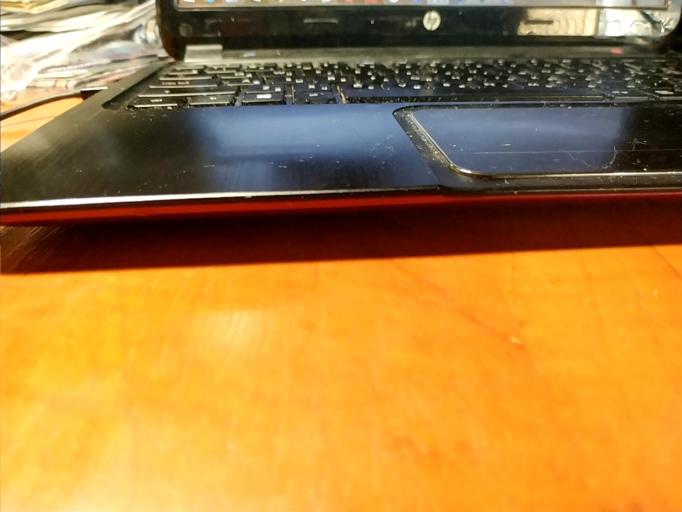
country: RU
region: Republic of Karelia
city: Belomorsk
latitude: 64.4968
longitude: 36.2623
